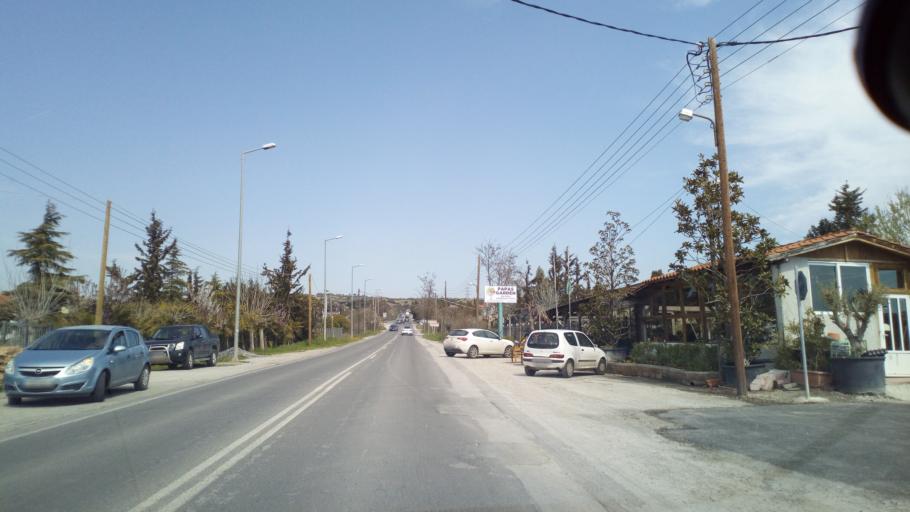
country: GR
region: Central Macedonia
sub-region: Nomos Thessalonikis
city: Thermi
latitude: 40.5584
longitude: 23.0210
